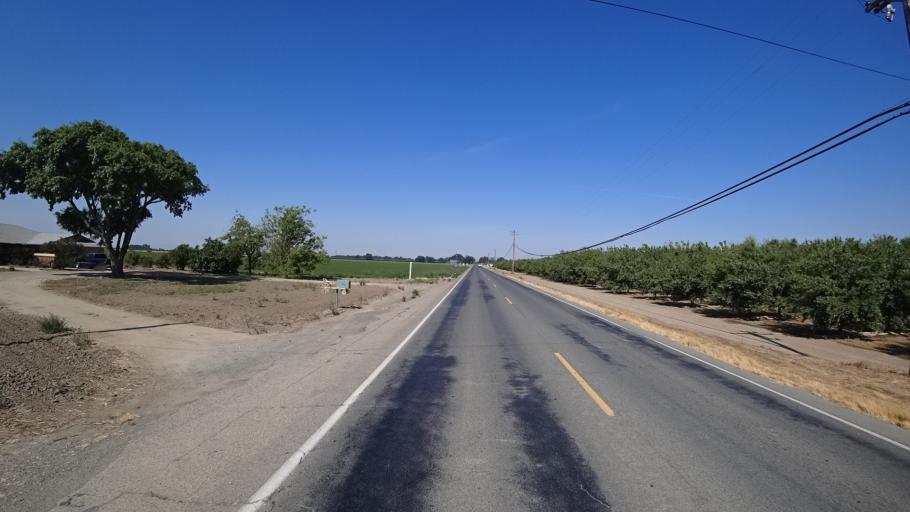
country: US
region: California
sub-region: Kings County
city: Lemoore
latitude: 36.3424
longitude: -119.8133
